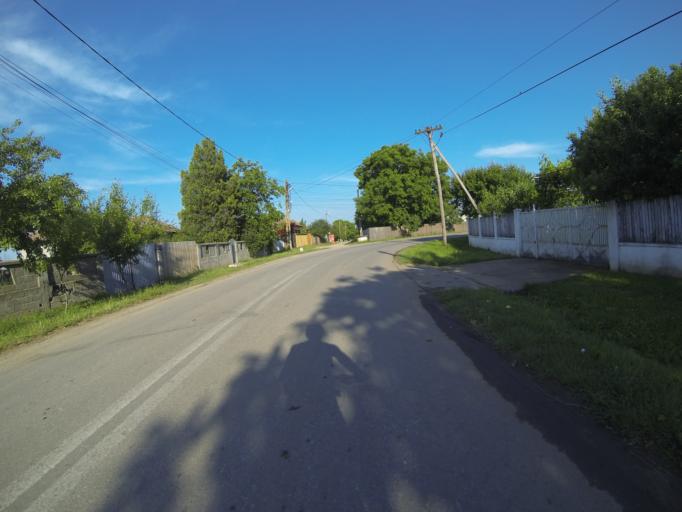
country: RO
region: Dolj
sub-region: Comuna Caloparu
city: Calopar
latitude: 44.1638
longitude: 23.7634
